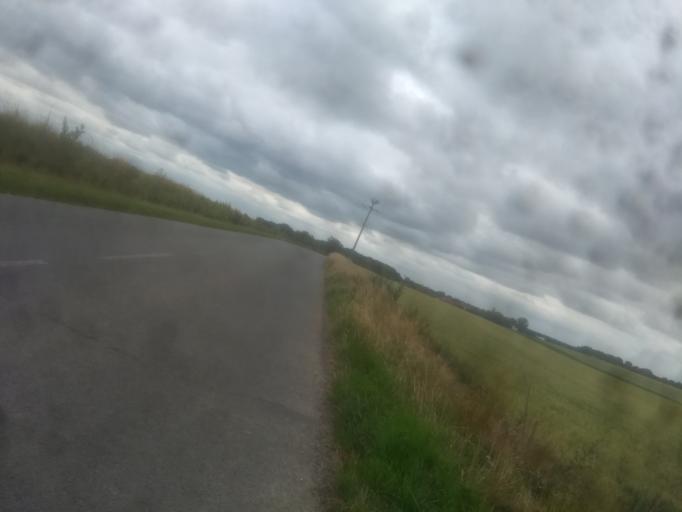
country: FR
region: Nord-Pas-de-Calais
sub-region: Departement du Pas-de-Calais
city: Thelus
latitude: 50.3361
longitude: 2.7944
